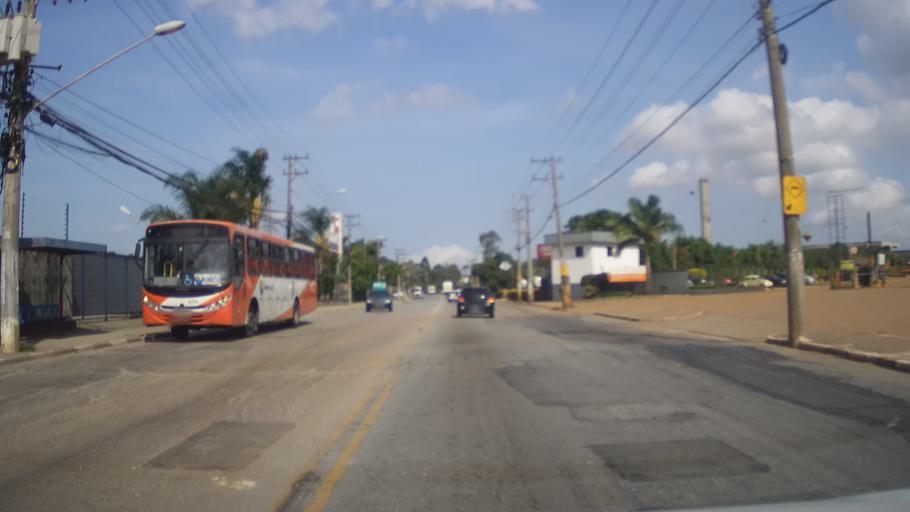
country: BR
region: Sao Paulo
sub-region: Guarulhos
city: Guarulhos
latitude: -23.4352
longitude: -46.4487
